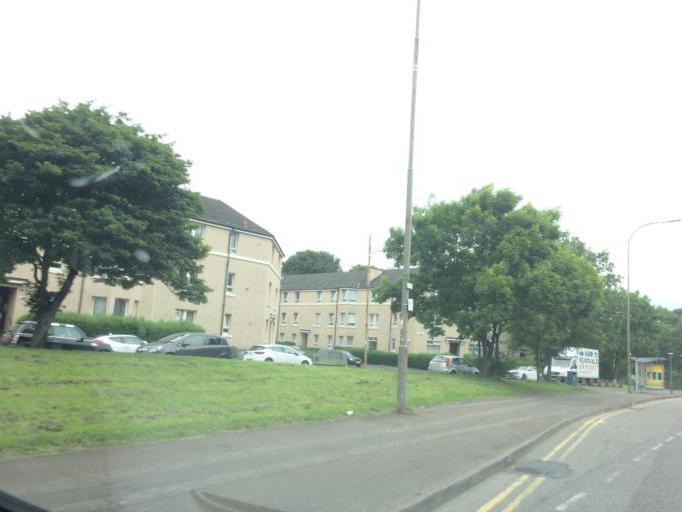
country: GB
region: Scotland
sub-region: East Renfrewshire
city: Giffnock
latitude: 55.8489
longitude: -4.3196
